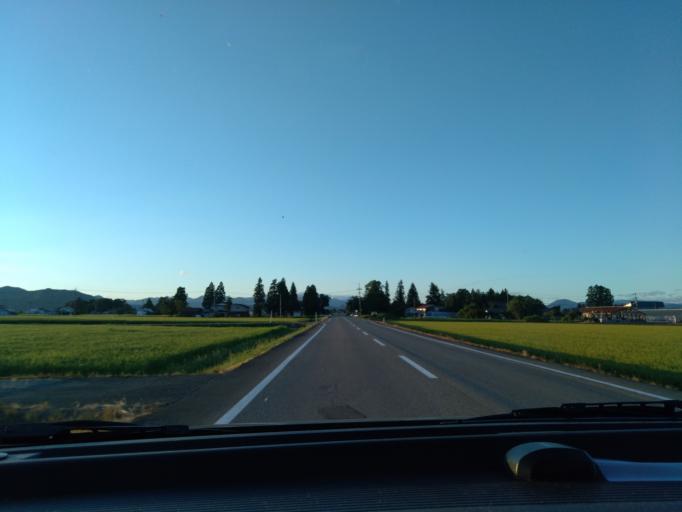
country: JP
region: Akita
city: Kakunodatemachi
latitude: 39.5083
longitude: 140.5594
